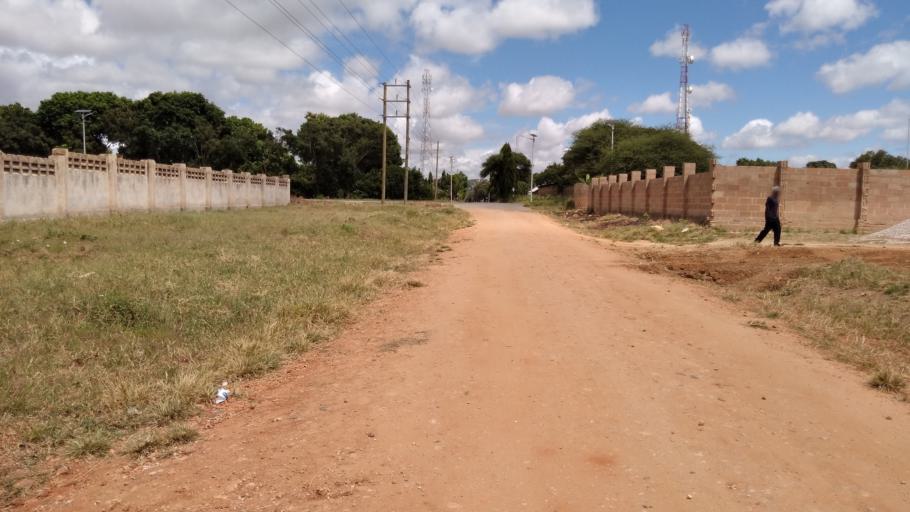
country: TZ
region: Dodoma
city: Dodoma
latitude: -6.1888
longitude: 35.7547
